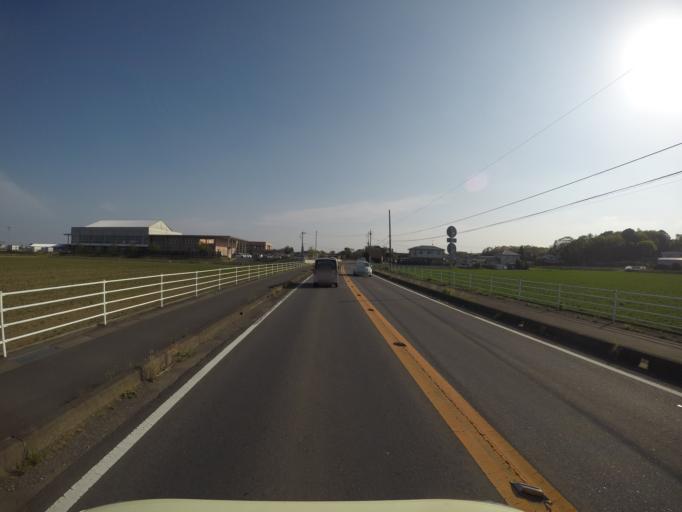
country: JP
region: Ibaraki
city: Ishige
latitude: 36.2024
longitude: 139.9763
